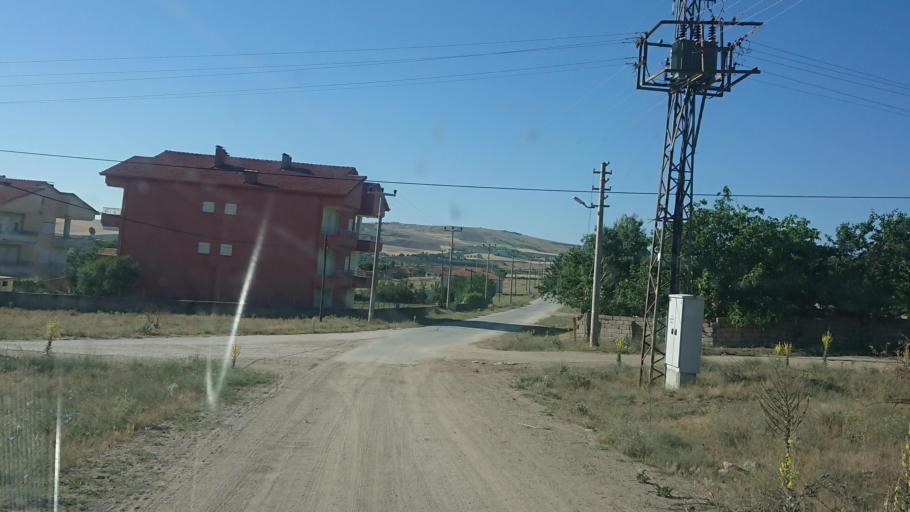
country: TR
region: Aksaray
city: Agacoren
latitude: 38.8721
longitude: 33.9444
